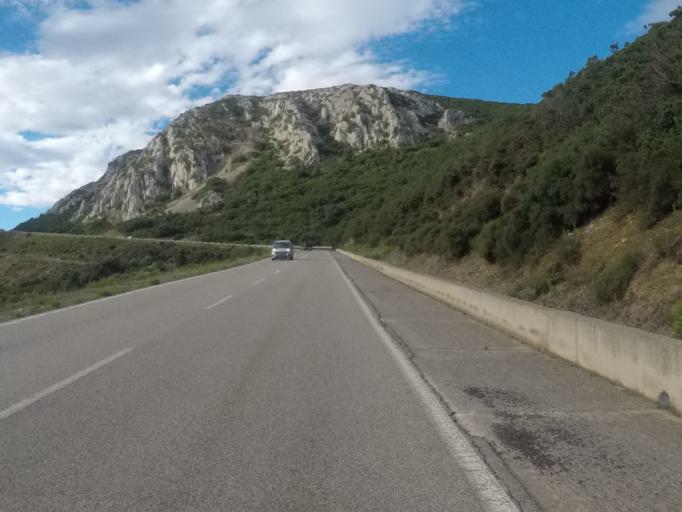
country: IT
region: Sardinia
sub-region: Provincia di Carbonia-Iglesias
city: Buggerru
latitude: 39.3508
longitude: 8.4380
